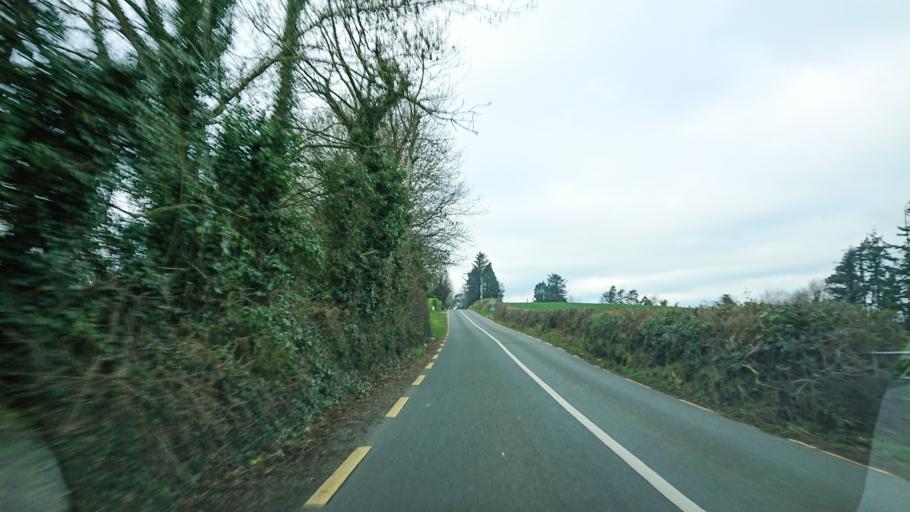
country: IE
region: Munster
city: Carrick-on-Suir
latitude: 52.3008
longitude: -7.4810
